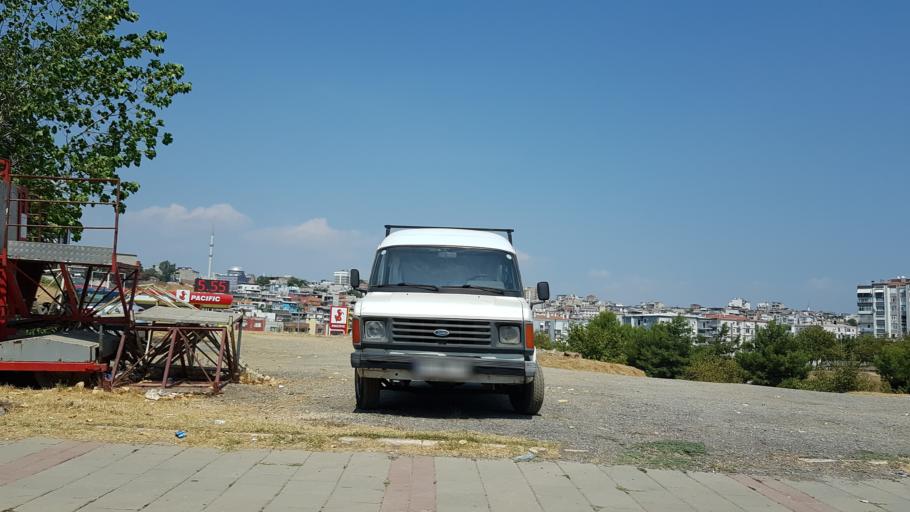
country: TR
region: Izmir
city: Karabaglar
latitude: 38.3706
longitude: 27.1082
